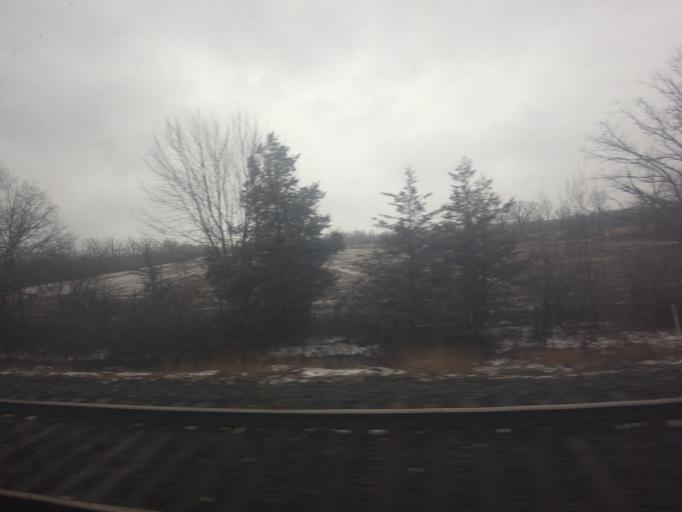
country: CA
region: Ontario
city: Belleville
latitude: 44.2036
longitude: -77.2577
